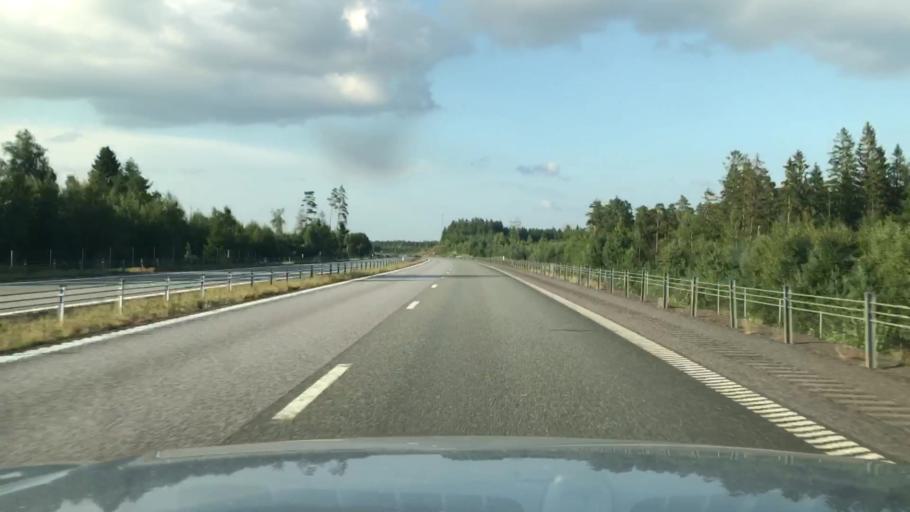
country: SE
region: Kronoberg
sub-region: Markaryds Kommun
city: Markaryd
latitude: 56.3986
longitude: 13.5332
